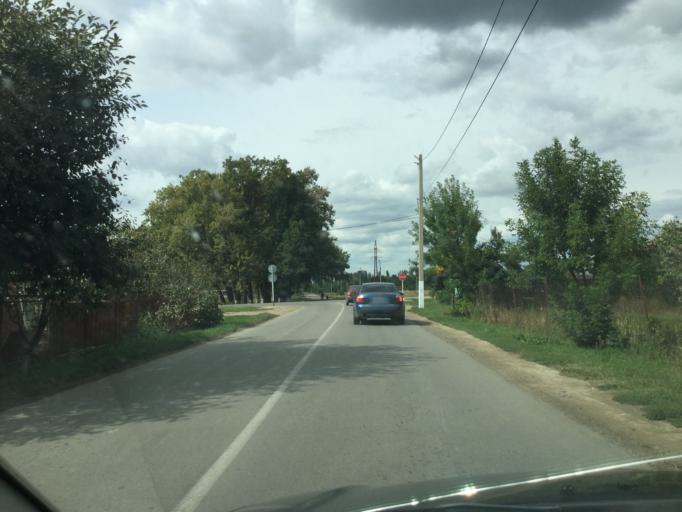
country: RU
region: Krasnodarskiy
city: Sovkhoznyy
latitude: 45.2754
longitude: 38.0958
